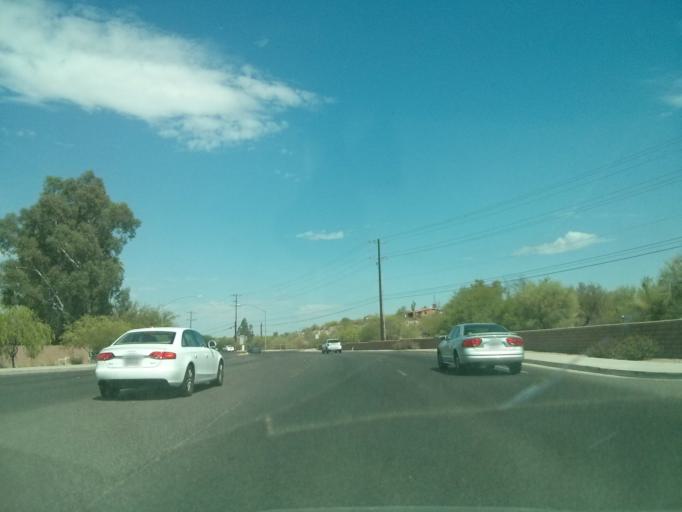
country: US
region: Arizona
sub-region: Pima County
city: Catalina Foothills
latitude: 32.2861
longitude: -110.9355
